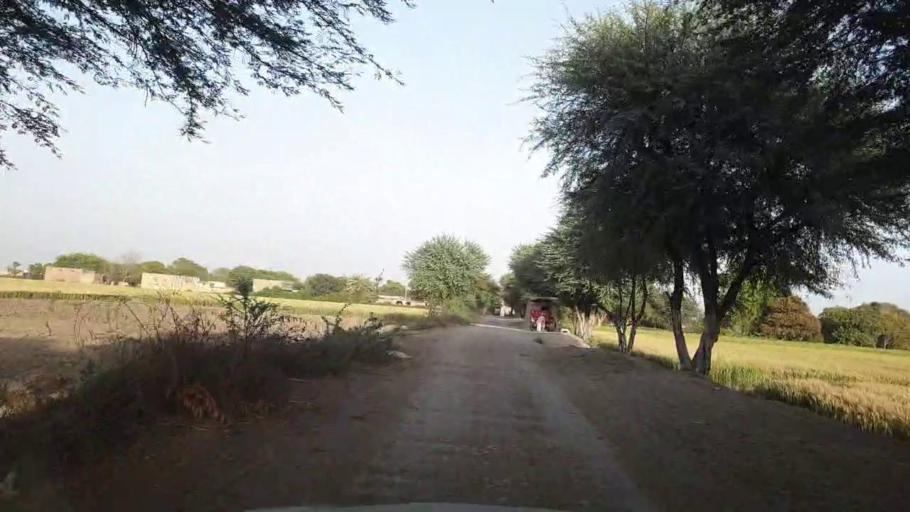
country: PK
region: Sindh
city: Tando Ghulam Ali
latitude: 25.1196
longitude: 68.9220
